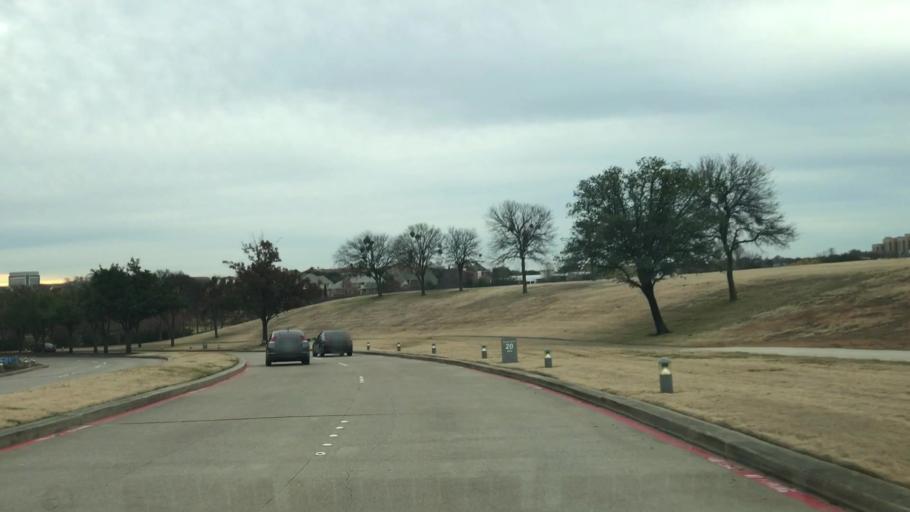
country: US
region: Texas
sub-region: Dallas County
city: Irving
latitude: 32.8761
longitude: -96.9564
